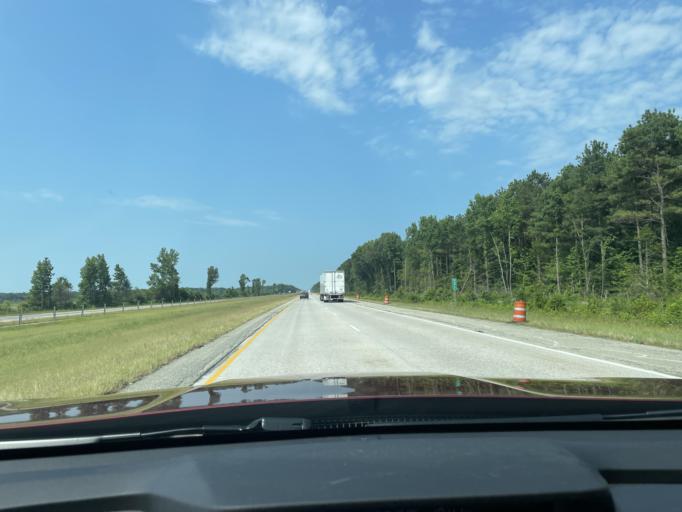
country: US
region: Arkansas
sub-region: White County
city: Searcy
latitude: 35.1507
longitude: -91.7930
